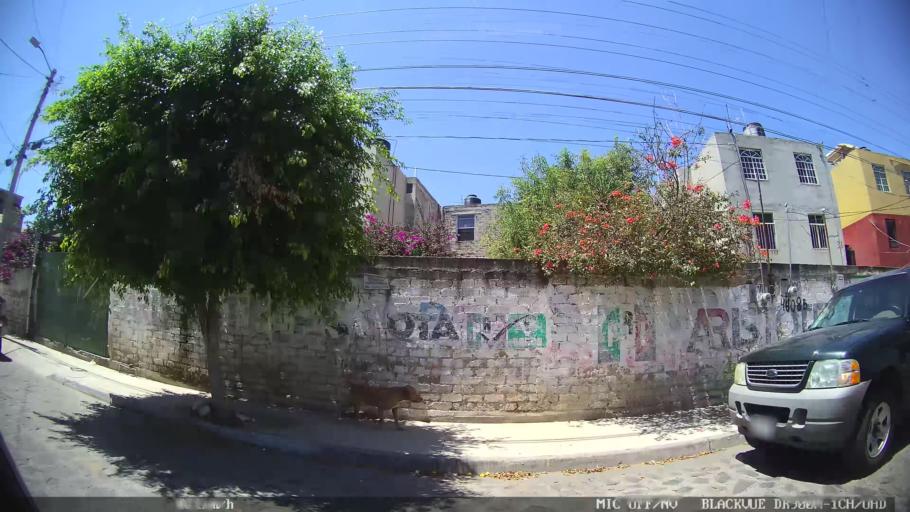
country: MX
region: Jalisco
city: Tlaquepaque
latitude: 20.6811
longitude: -103.2791
